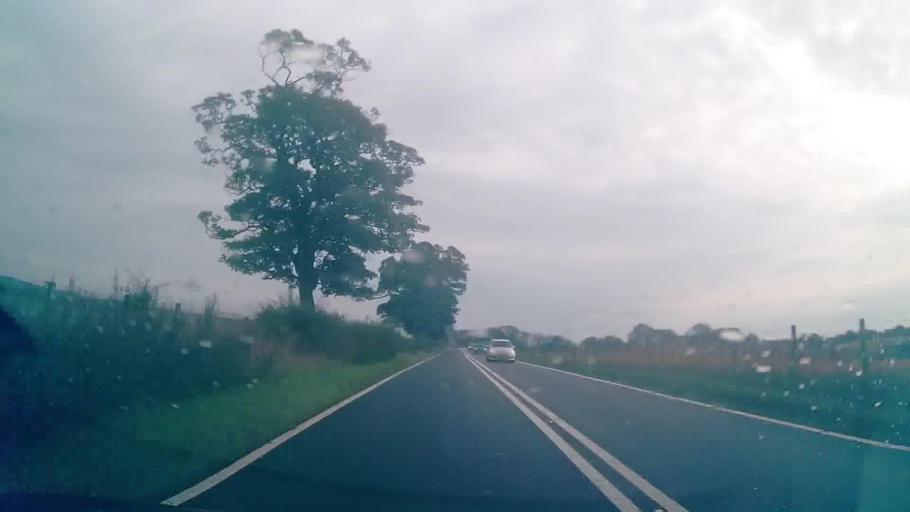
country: GB
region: Scotland
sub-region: Dumfries and Galloway
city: Lochmaben
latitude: 55.0641
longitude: -3.5004
